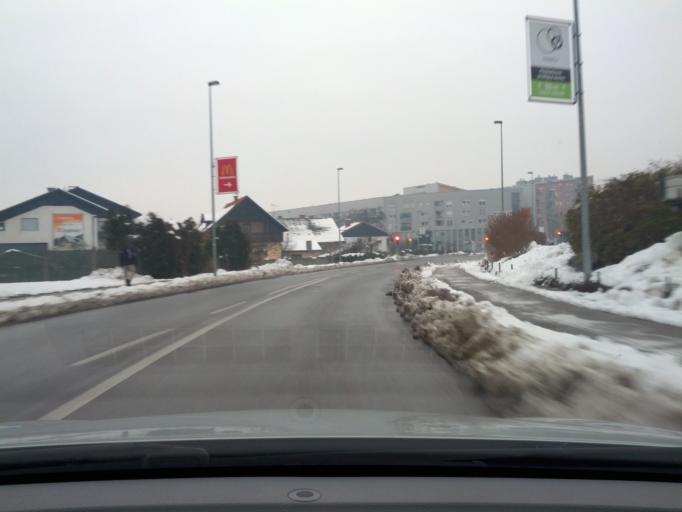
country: SI
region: Domzale
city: Domzale
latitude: 46.1364
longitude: 14.6000
